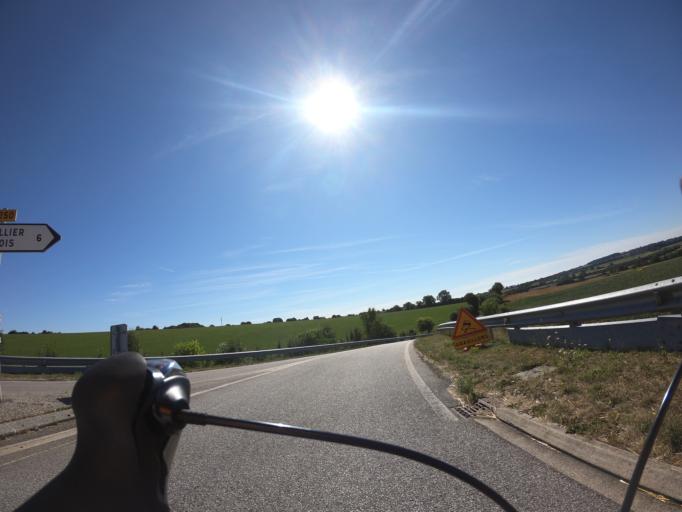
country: FR
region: Pays de la Loire
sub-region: Departement de la Mayenne
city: Pre-en-Pail
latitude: 48.5644
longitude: -0.1378
